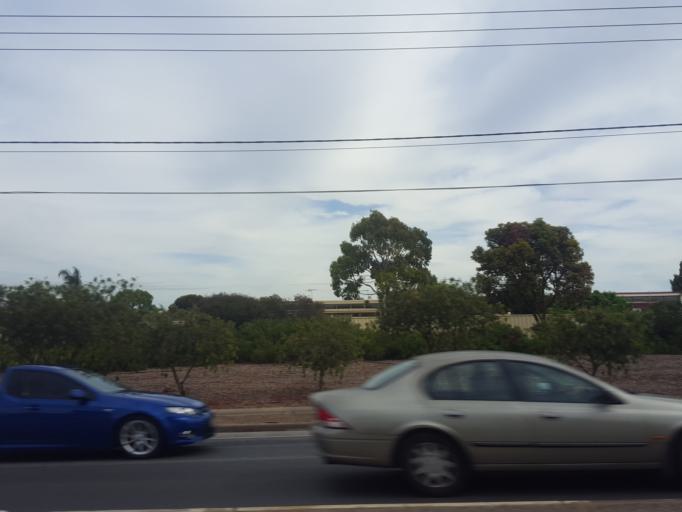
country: AU
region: South Australia
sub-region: Port Adelaide Enfield
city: Alberton
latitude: -34.8511
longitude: 138.5347
